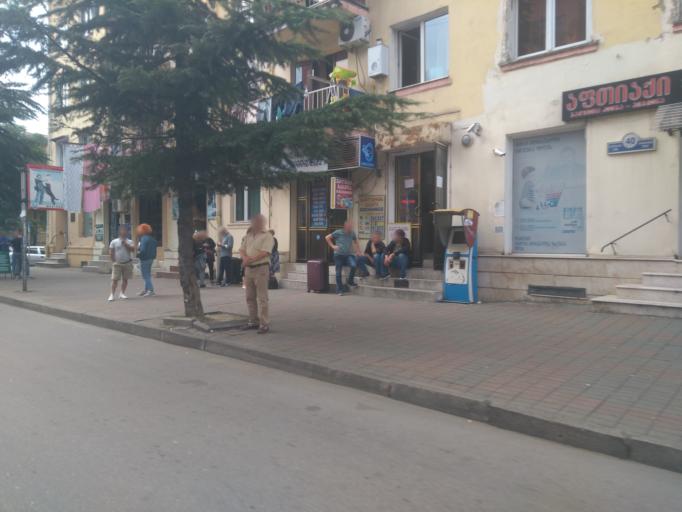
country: GE
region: Ajaria
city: Batumi
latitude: 41.6442
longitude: 41.6340
